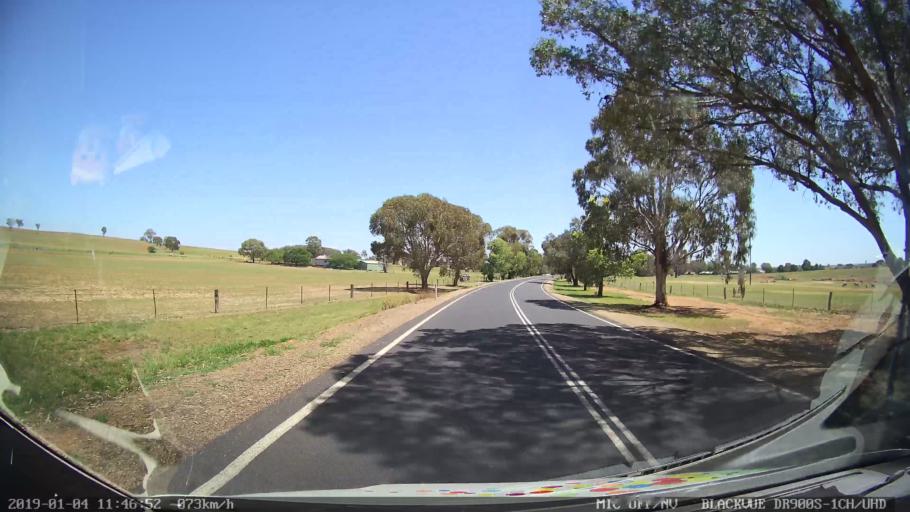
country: AU
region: New South Wales
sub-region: Cabonne
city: Molong
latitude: -32.9375
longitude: 148.7566
